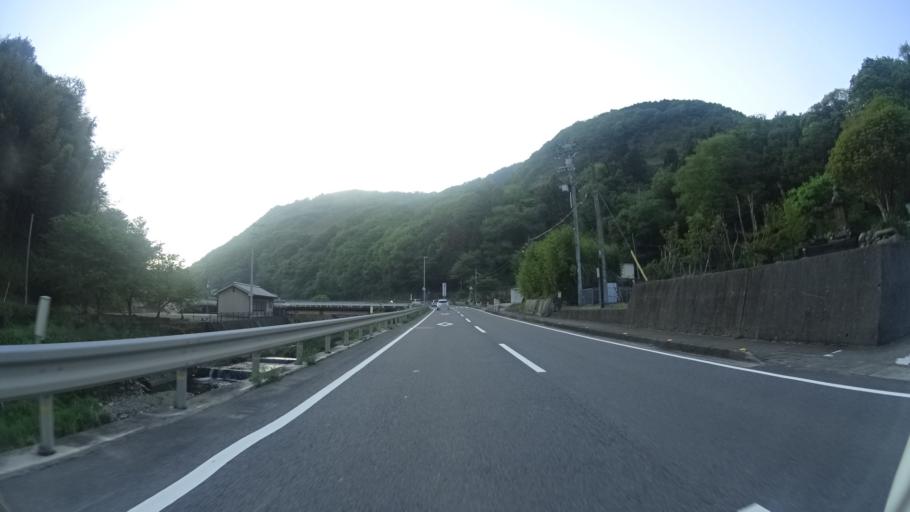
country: JP
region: Tokushima
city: Ikedacho
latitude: 34.0095
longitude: 133.7316
